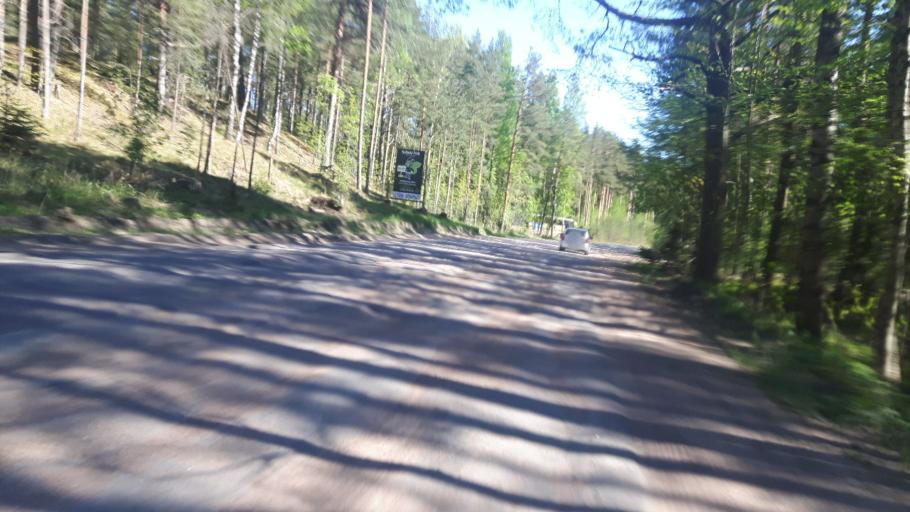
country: RU
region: Leningrad
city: Glebychevo
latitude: 60.2420
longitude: 29.0002
